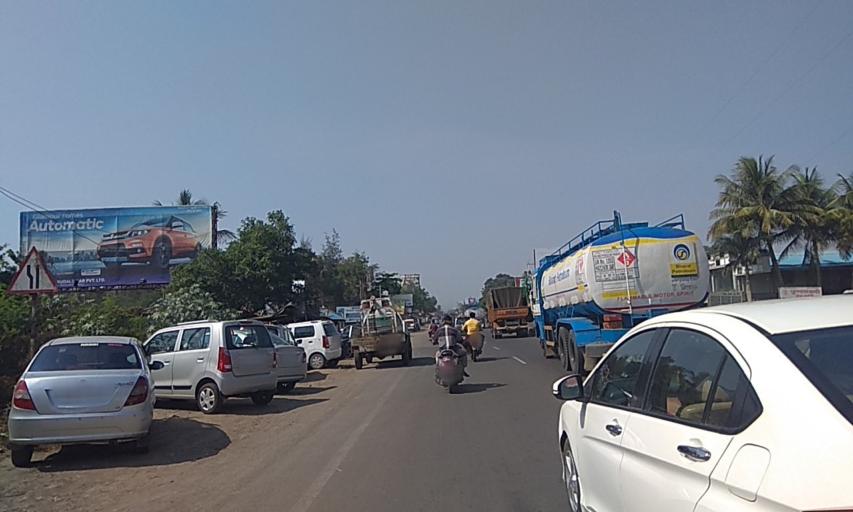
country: IN
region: Maharashtra
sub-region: Pune Division
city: Lohogaon
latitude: 18.4950
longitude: 73.9794
